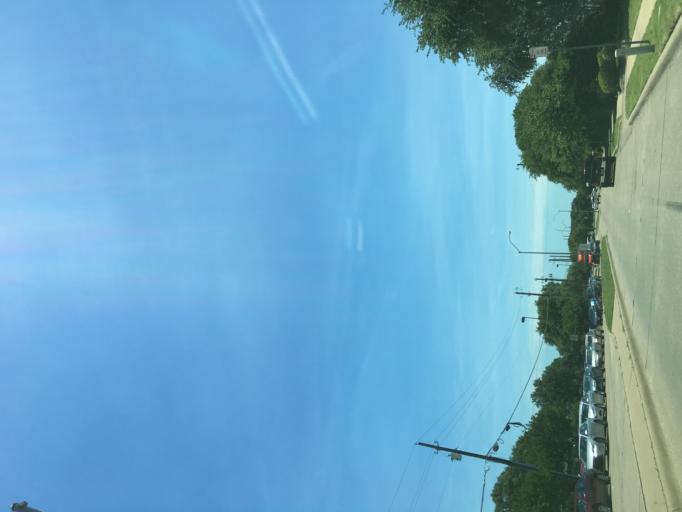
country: US
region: Texas
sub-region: Dallas County
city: Richardson
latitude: 32.9676
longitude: -96.7241
